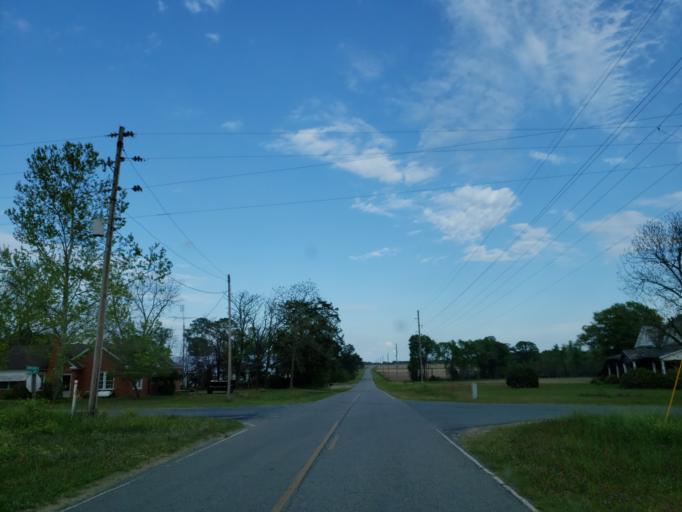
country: US
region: Georgia
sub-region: Dooly County
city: Vienna
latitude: 32.1234
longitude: -83.7140
